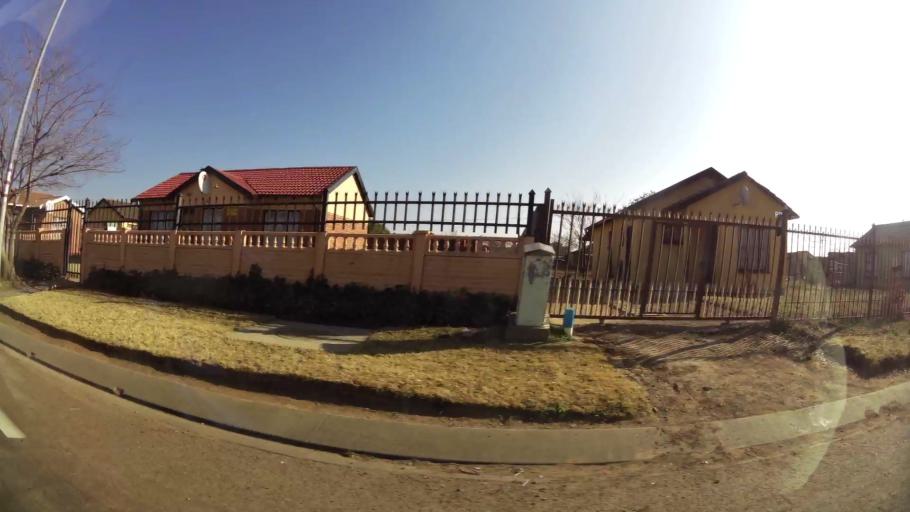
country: ZA
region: Orange Free State
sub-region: Mangaung Metropolitan Municipality
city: Bloemfontein
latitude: -29.1864
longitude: 26.1760
